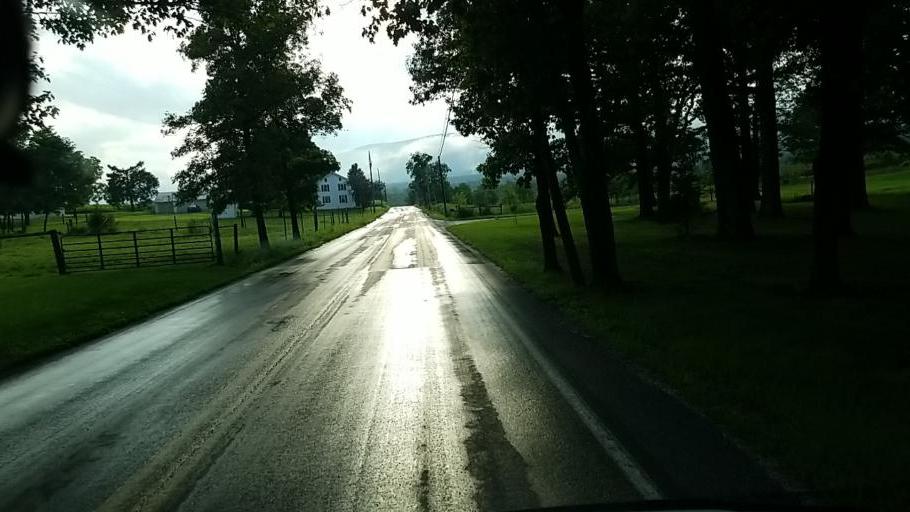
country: US
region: Pennsylvania
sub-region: Cumberland County
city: Newville
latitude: 40.1885
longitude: -77.5216
